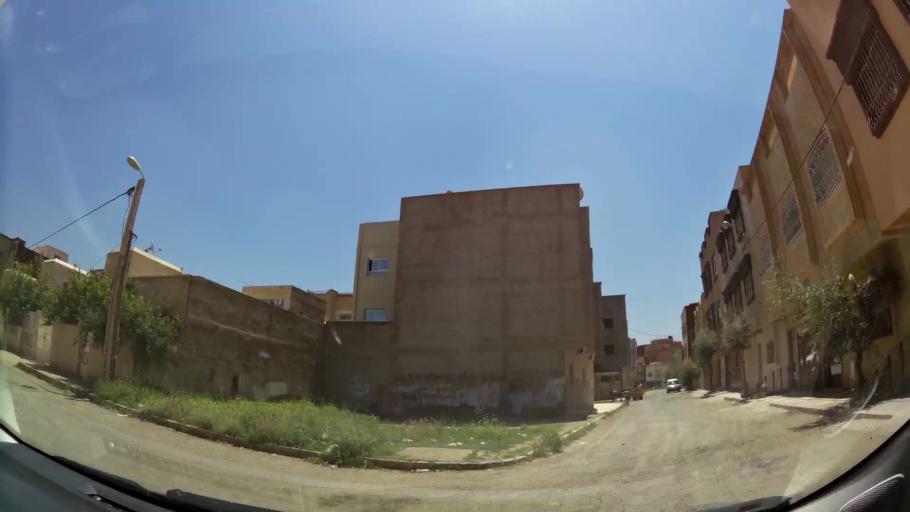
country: MA
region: Oriental
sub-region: Oujda-Angad
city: Oujda
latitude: 34.6660
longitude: -1.9454
